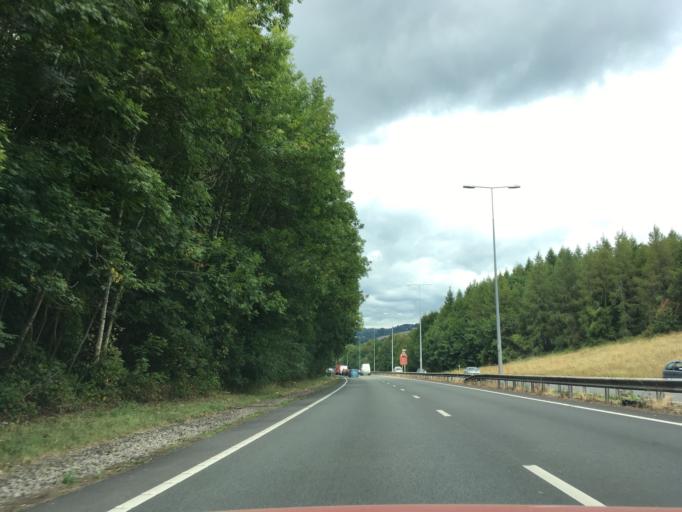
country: GB
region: Wales
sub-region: Torfaen County Borough
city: New Inn
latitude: 51.6764
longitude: -3.0092
